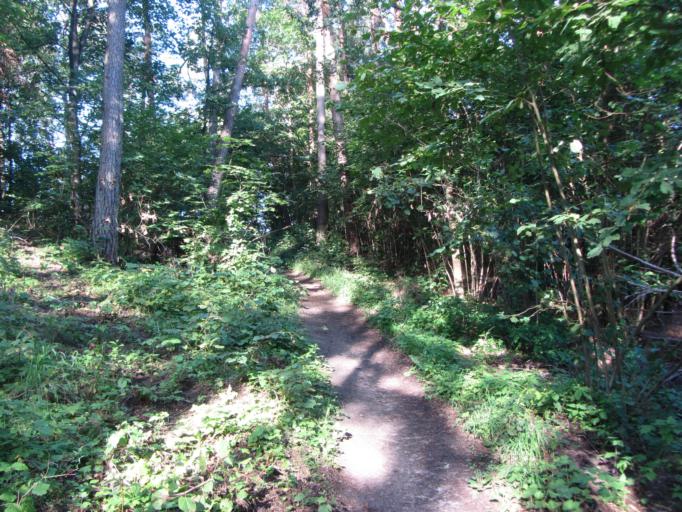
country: LT
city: Birstonas
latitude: 54.6048
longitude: 24.0081
